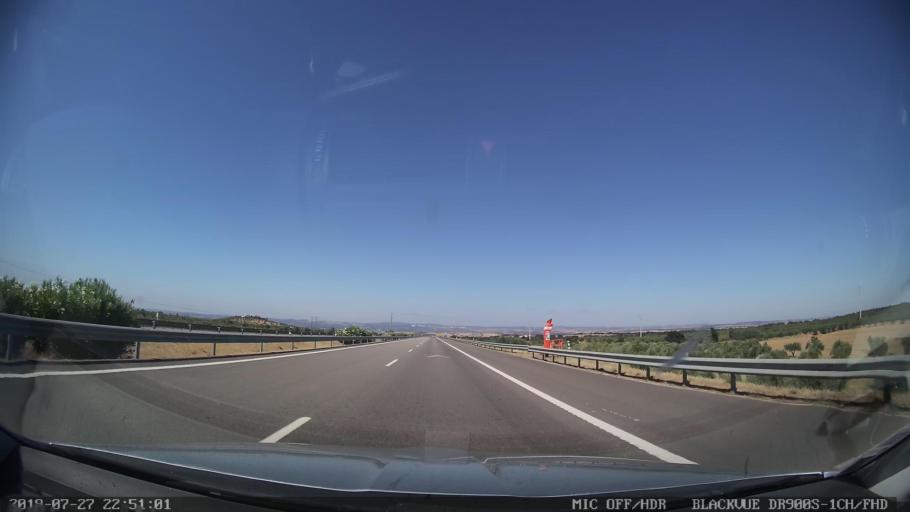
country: PT
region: Portalegre
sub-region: Elvas
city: Elvas
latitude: 38.8738
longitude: -7.2713
